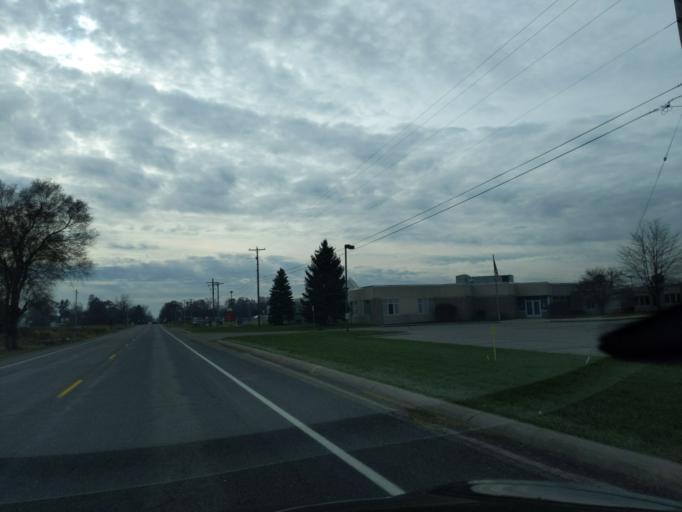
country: US
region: Michigan
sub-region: Ingham County
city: Holt
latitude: 42.5861
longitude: -84.5230
